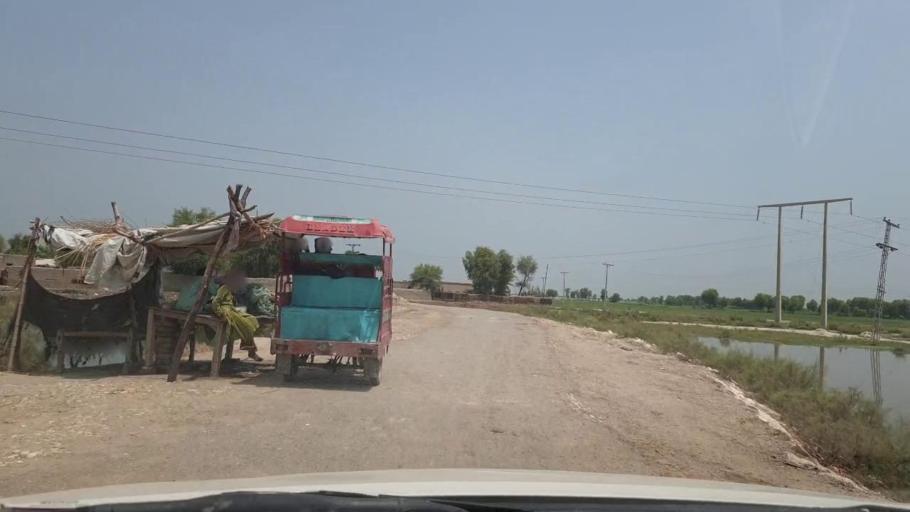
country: PK
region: Sindh
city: Rustam jo Goth
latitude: 28.0162
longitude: 68.7836
